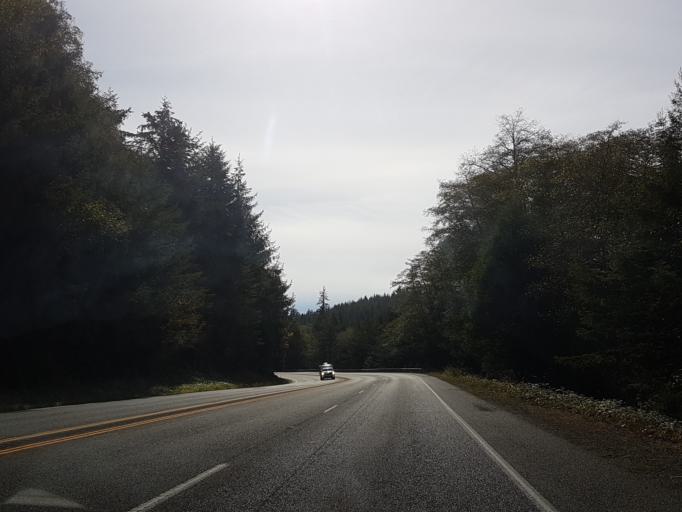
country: US
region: California
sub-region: Del Norte County
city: Bertsch-Oceanview
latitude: 41.4879
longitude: -124.0500
